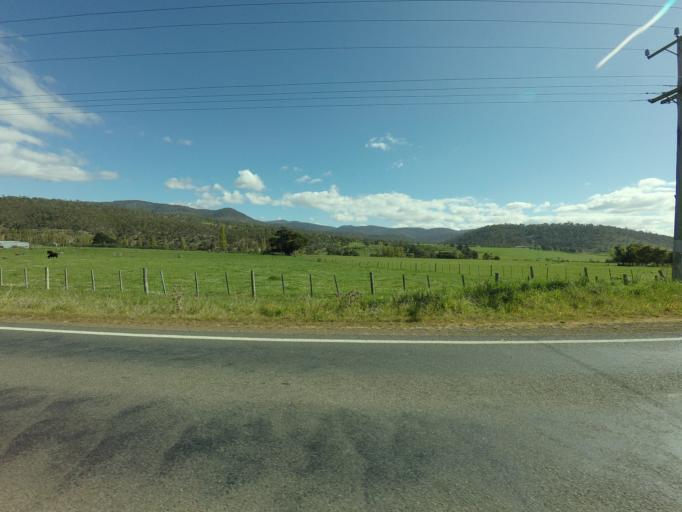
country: AU
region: Tasmania
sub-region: Derwent Valley
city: New Norfolk
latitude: -42.7720
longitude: 147.0330
